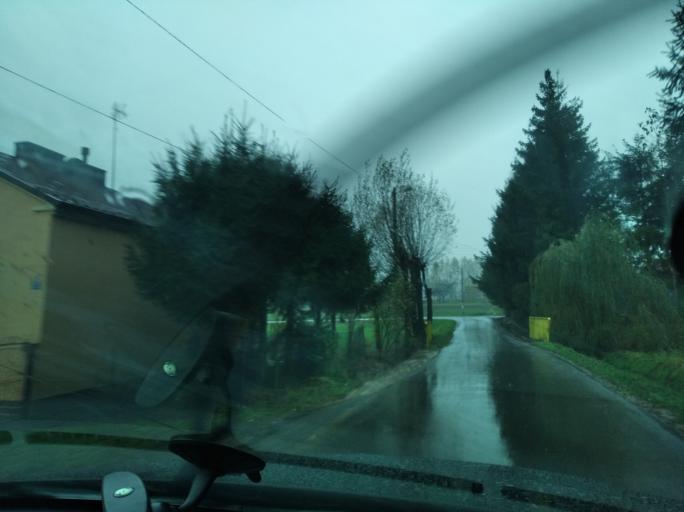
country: PL
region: Subcarpathian Voivodeship
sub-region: Powiat lancucki
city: Albigowa
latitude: 50.0386
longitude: 22.2181
